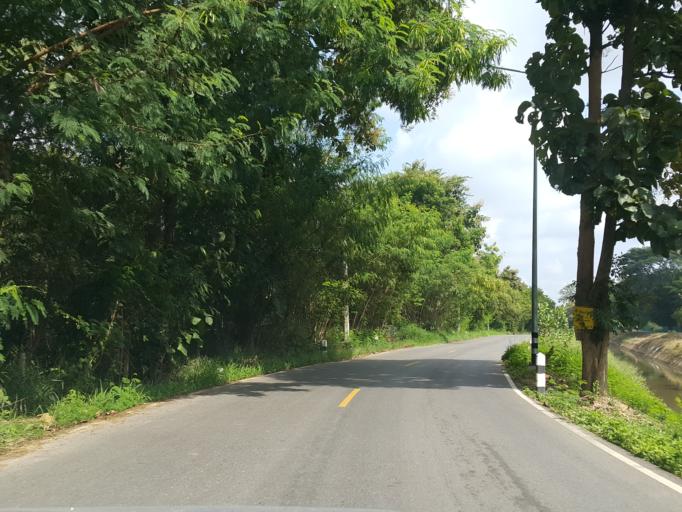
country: TH
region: Chiang Mai
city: San Sai
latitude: 18.9084
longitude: 99.0124
